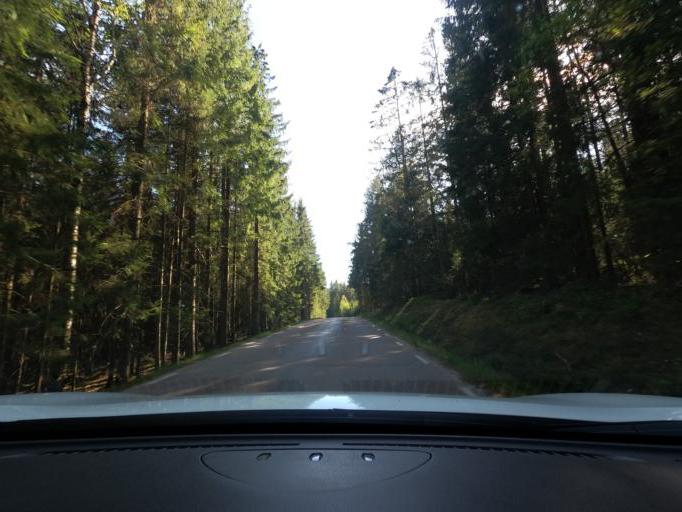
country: SE
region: Vaestra Goetaland
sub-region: Harryda Kommun
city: Hindas
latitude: 57.6358
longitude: 12.3363
